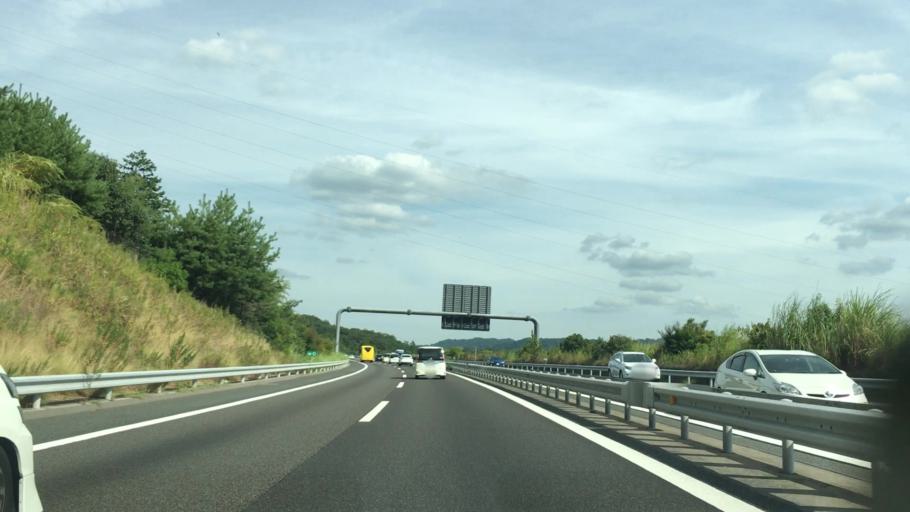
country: JP
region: Shiga Prefecture
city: Kusatsu
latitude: 34.9650
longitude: 135.9642
